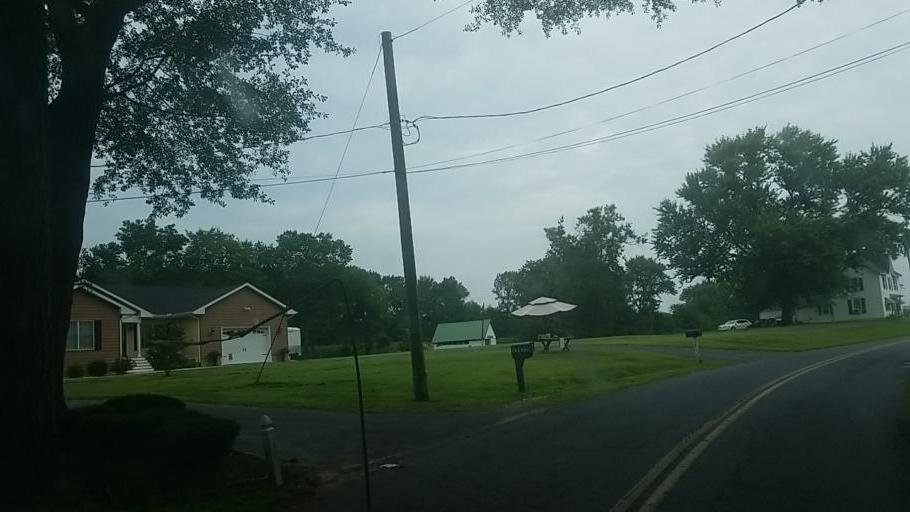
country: US
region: Delaware
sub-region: Sussex County
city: Selbyville
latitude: 38.4352
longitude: -75.1947
